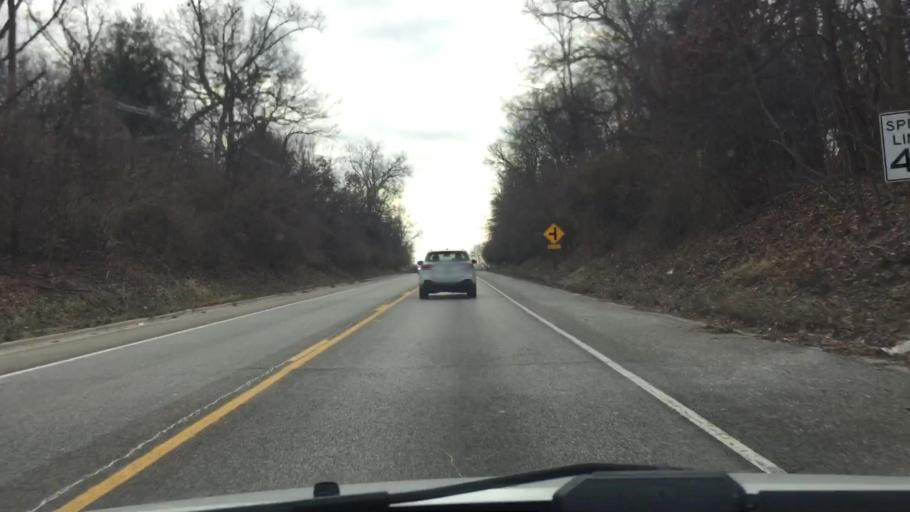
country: US
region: Illinois
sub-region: McHenry County
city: Prairie Grove
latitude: 42.2622
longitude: -88.2868
